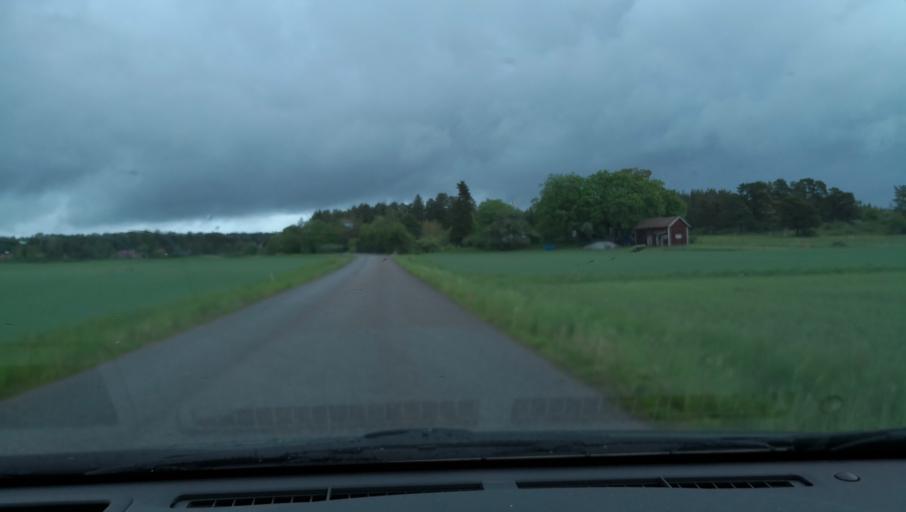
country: SE
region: Uppsala
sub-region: Enkopings Kommun
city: Orsundsbro
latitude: 59.8129
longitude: 17.3859
